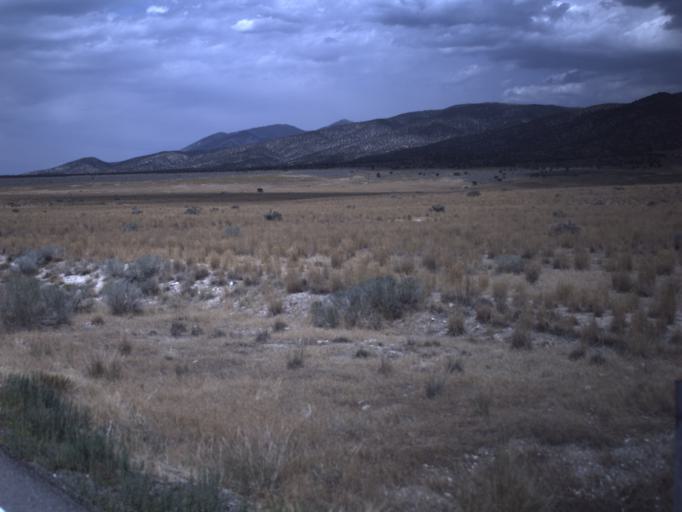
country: US
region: Utah
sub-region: Utah County
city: Eagle Mountain
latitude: 40.2681
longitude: -112.2411
